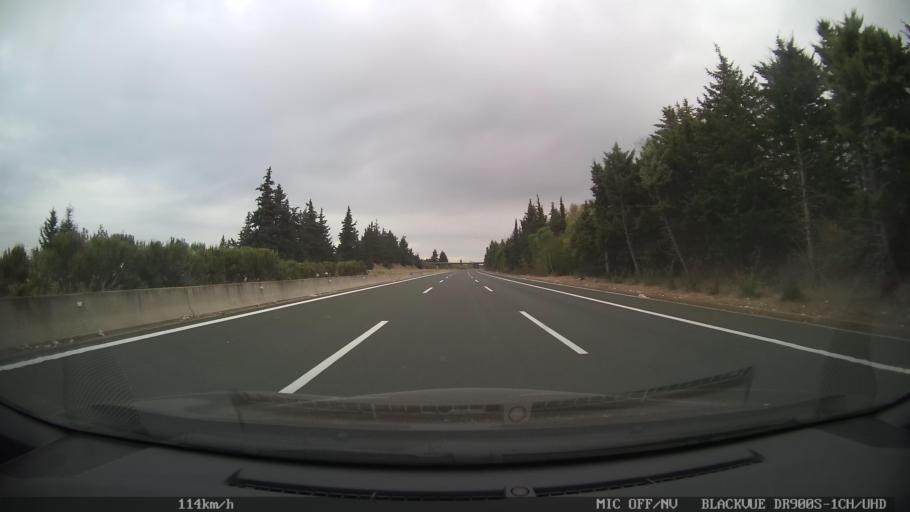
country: GR
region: Central Macedonia
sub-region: Nomos Pierias
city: Makrygialos
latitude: 40.3983
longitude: 22.6007
